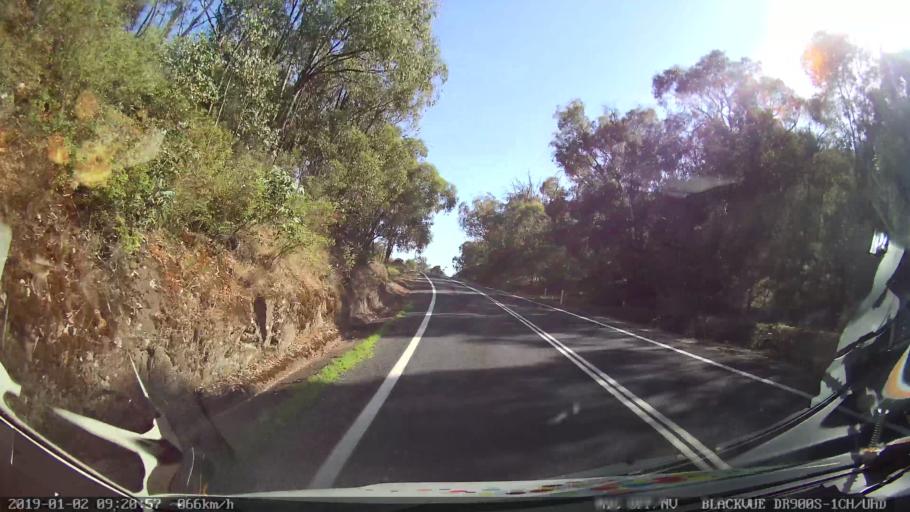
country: AU
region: New South Wales
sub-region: Tumut Shire
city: Tumut
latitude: -35.4110
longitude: 148.2892
